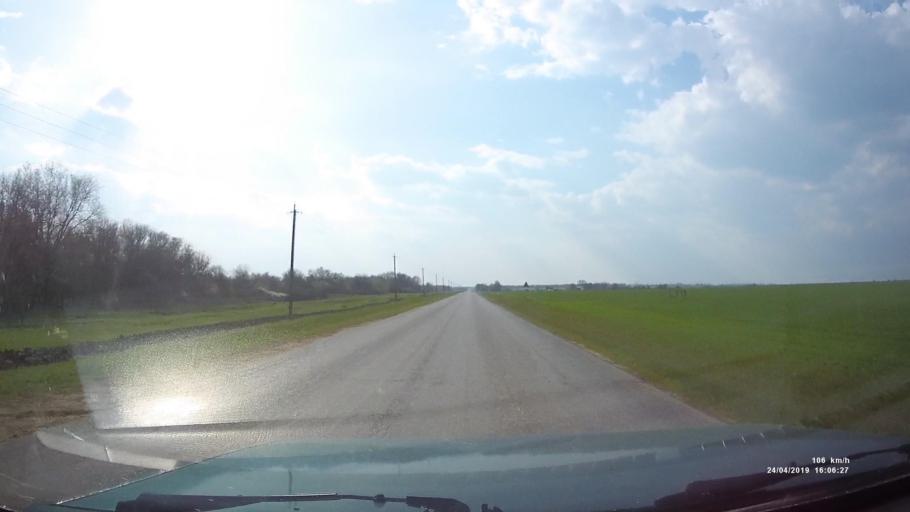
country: RU
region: Rostov
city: Sovetskoye
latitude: 46.6866
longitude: 42.3486
